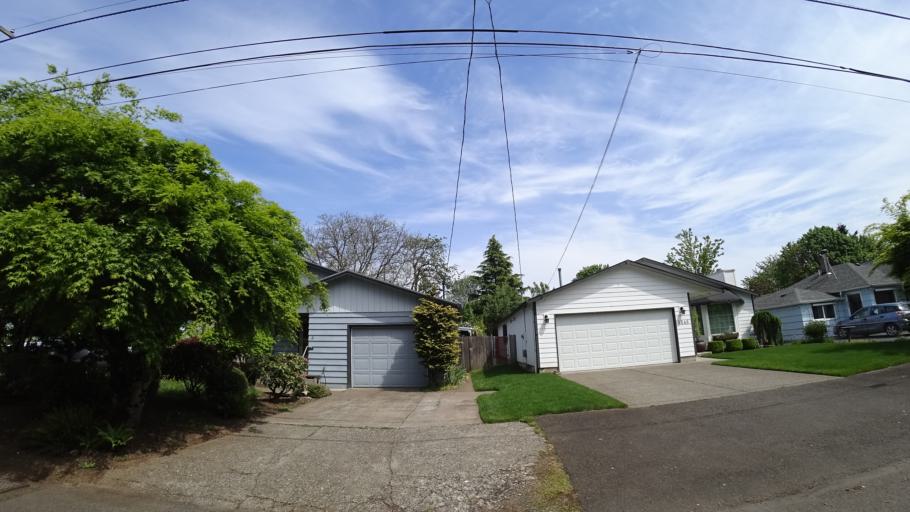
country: US
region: Oregon
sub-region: Multnomah County
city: Lents
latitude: 45.4751
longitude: -122.6059
